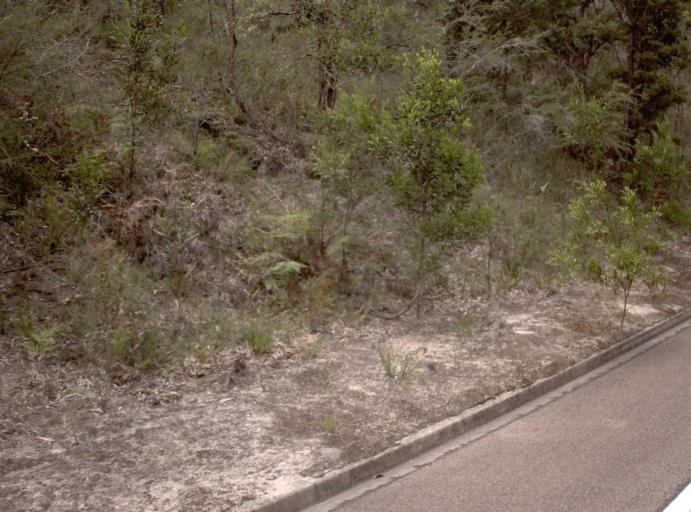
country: AU
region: New South Wales
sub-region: Bega Valley
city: Eden
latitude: -37.3999
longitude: 149.6706
